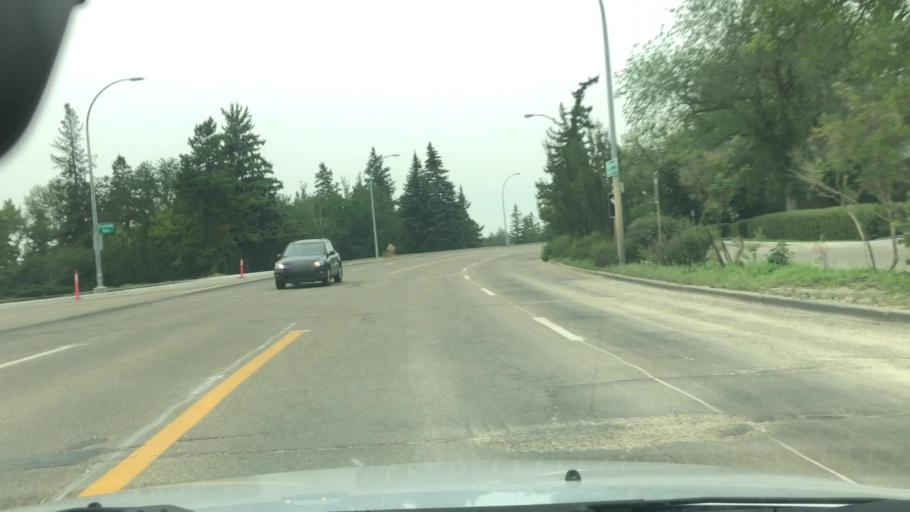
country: CA
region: Alberta
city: Edmonton
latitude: 53.5183
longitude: -113.5362
